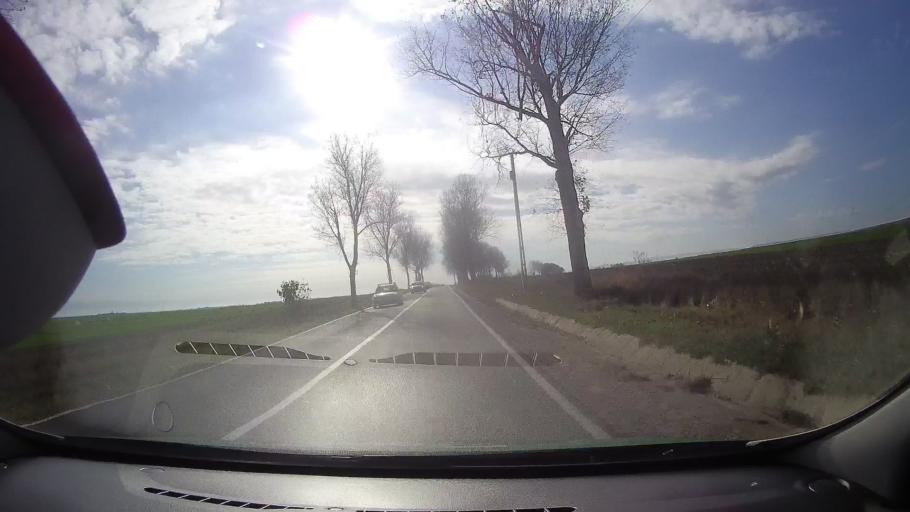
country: RO
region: Tulcea
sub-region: Comuna Valea Nucarilor
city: Agighiol
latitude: 44.9984
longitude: 28.8863
